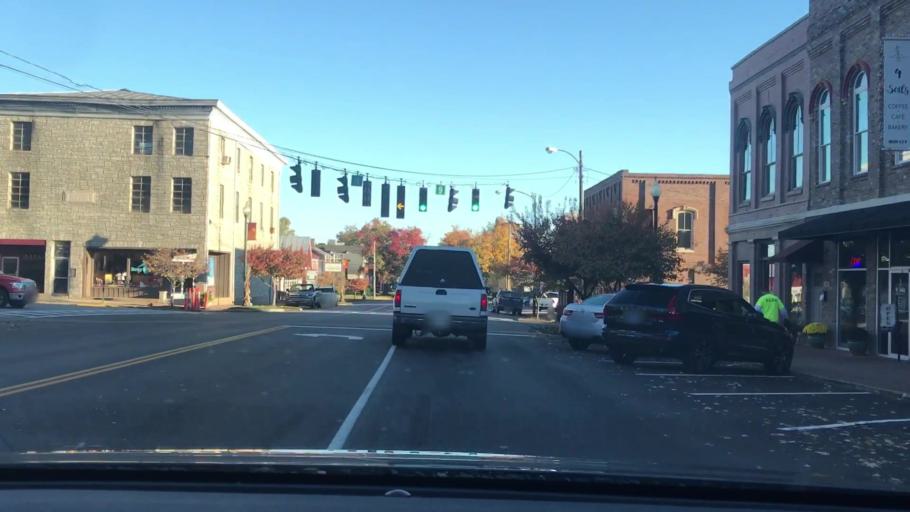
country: US
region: Kentucky
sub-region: Simpson County
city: Franklin
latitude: 36.7228
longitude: -86.5779
